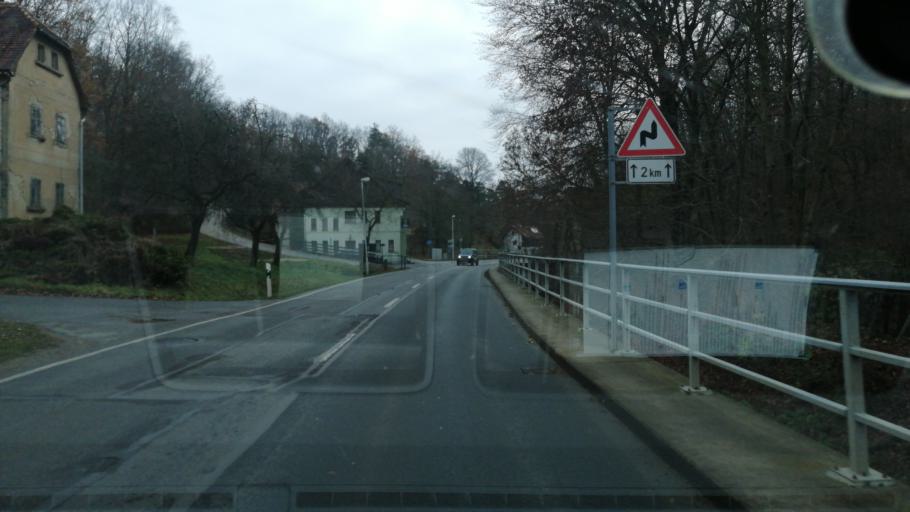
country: DE
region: Saxony
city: Bernstadt
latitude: 51.0611
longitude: 14.8080
